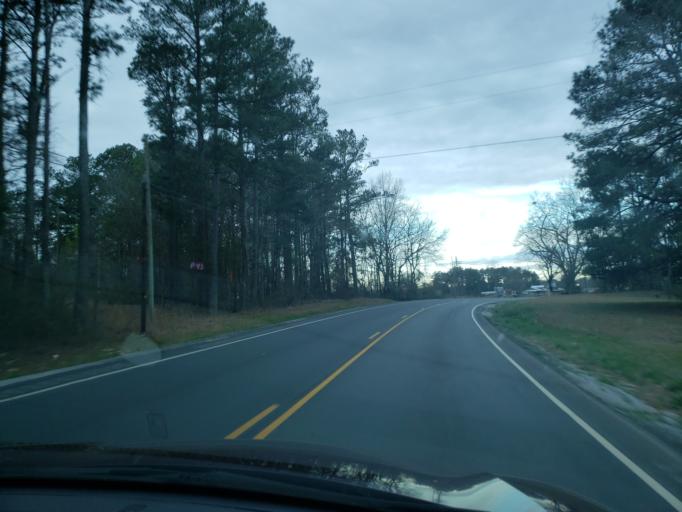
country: US
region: Alabama
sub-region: Randolph County
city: Roanoke
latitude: 33.1005
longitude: -85.3474
